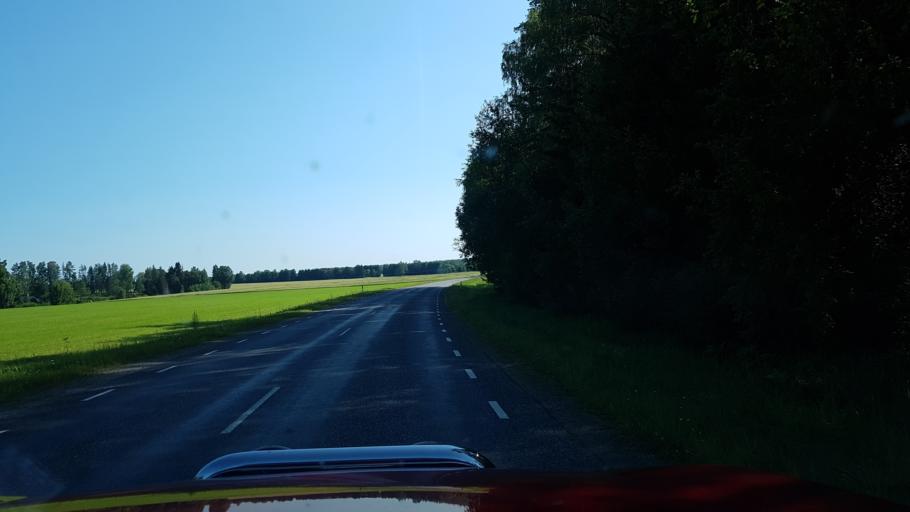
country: EE
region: Polvamaa
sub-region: Polva linn
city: Polva
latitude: 57.9974
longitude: 26.9130
